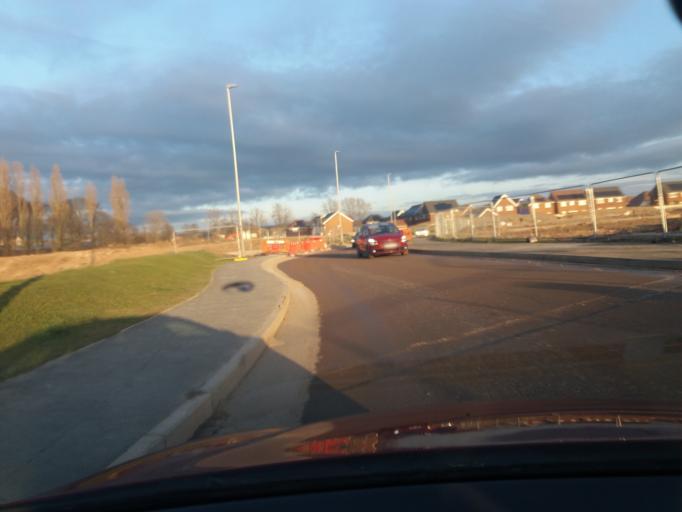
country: GB
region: England
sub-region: Lancashire
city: Euxton
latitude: 53.6759
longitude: -2.6704
